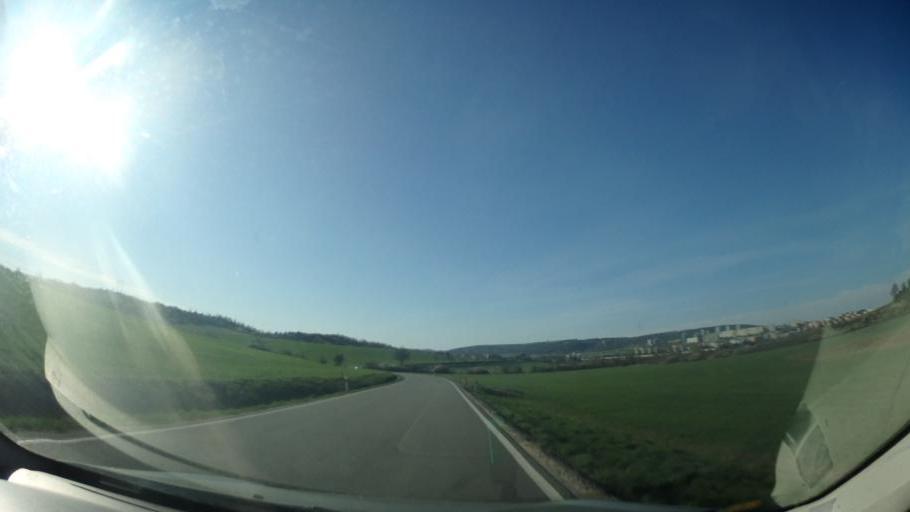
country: CZ
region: South Moravian
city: Ostopovice
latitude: 49.1530
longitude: 16.5571
